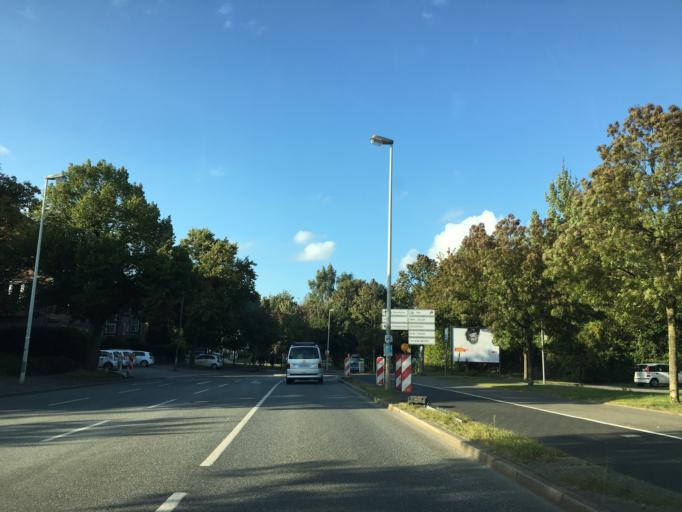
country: DE
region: Schleswig-Holstein
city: Altenholz
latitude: 54.3610
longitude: 10.1309
